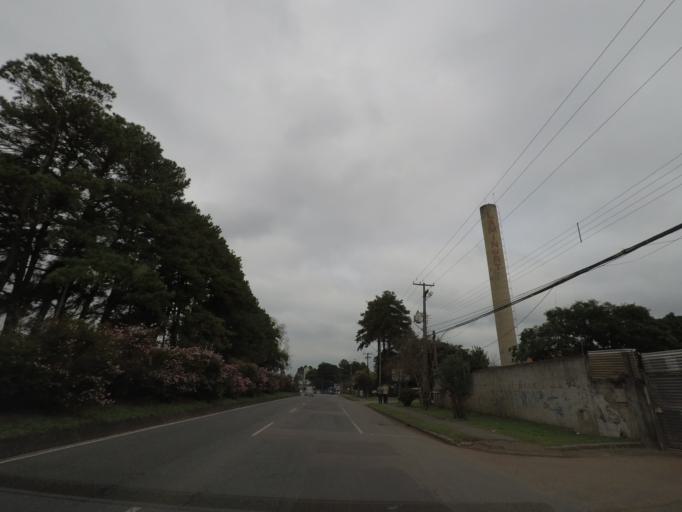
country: BR
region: Parana
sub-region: Curitiba
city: Curitiba
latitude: -25.4938
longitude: -49.3243
